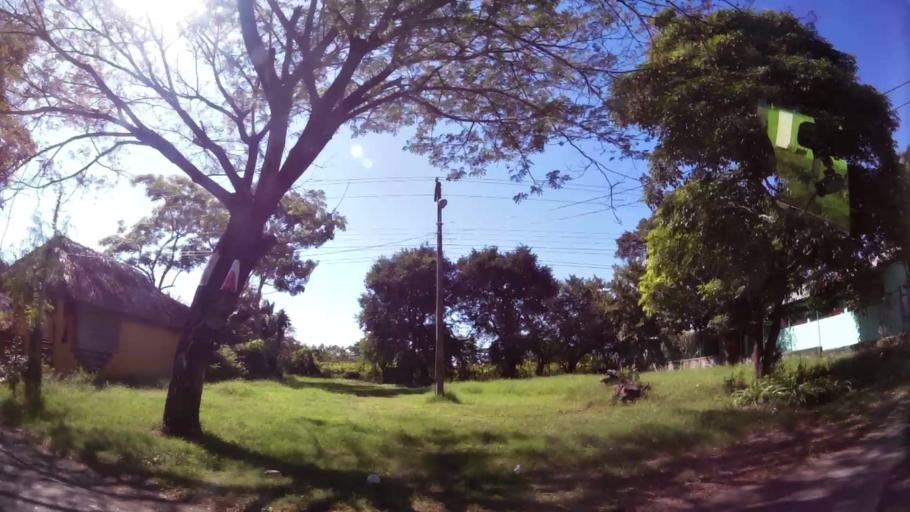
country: GT
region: Santa Rosa
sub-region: Municipio de Taxisco
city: Taxisco
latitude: 13.9106
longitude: -90.5280
